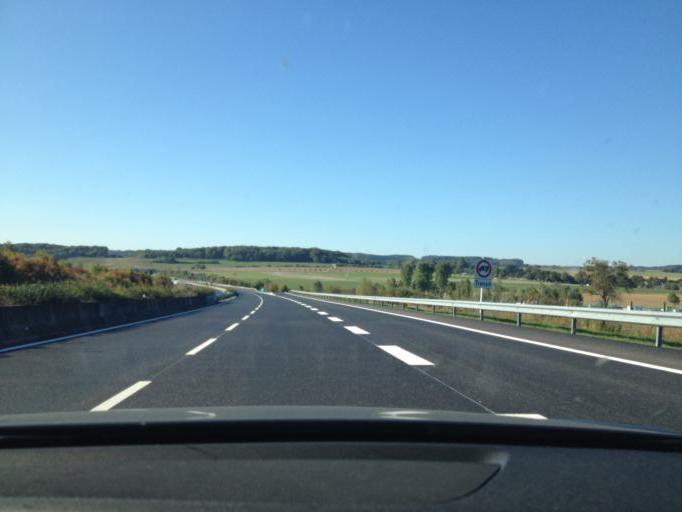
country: LU
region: Grevenmacher
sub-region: Canton de Remich
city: Mondorf-les-Bains
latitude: 49.5109
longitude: 6.2984
